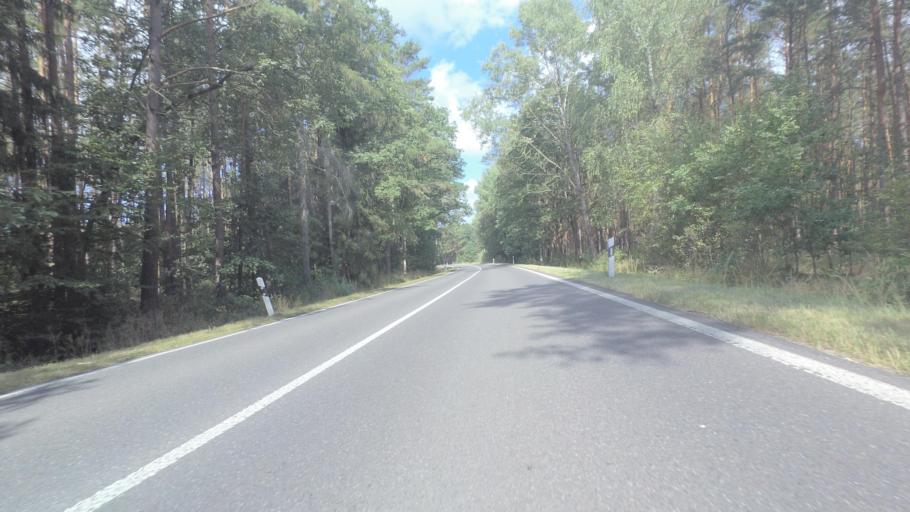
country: DE
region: Brandenburg
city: Walsleben
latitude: 52.9870
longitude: 12.6978
